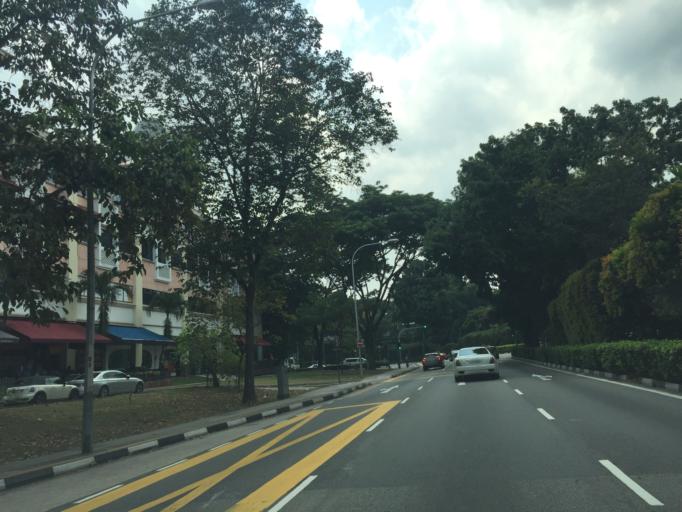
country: SG
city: Singapore
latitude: 1.3166
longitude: 103.8357
